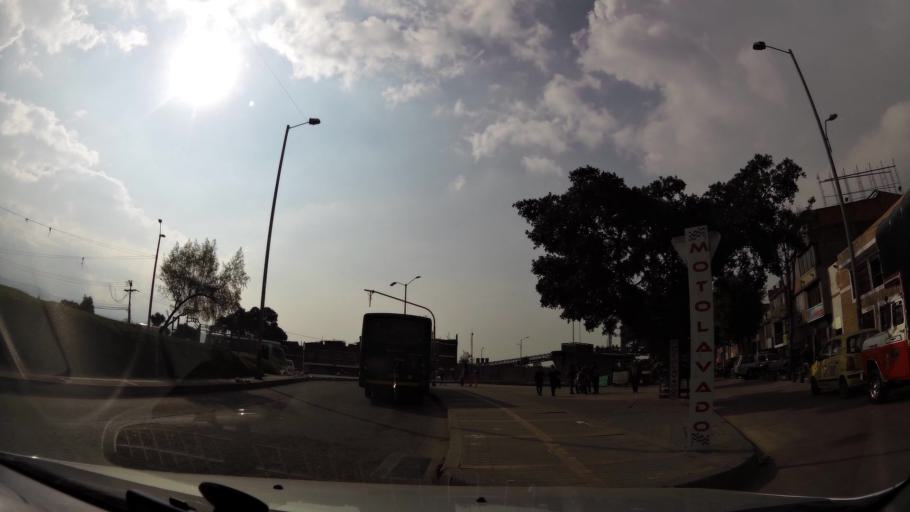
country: CO
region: Bogota D.C.
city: Bogota
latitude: 4.5552
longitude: -74.1209
